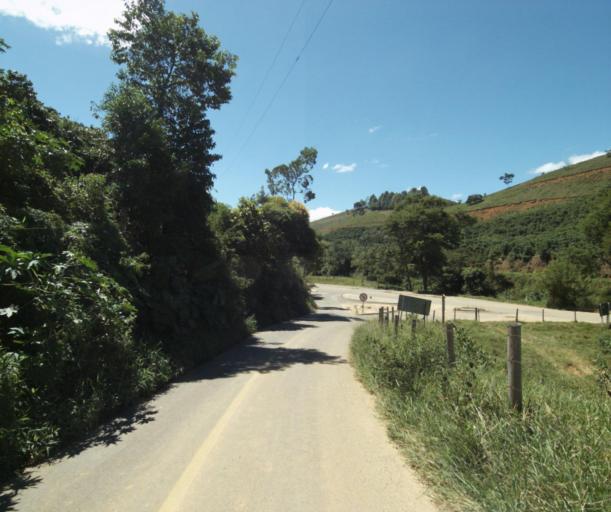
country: BR
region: Minas Gerais
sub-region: Espera Feliz
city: Espera Feliz
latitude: -20.6408
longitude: -41.8073
